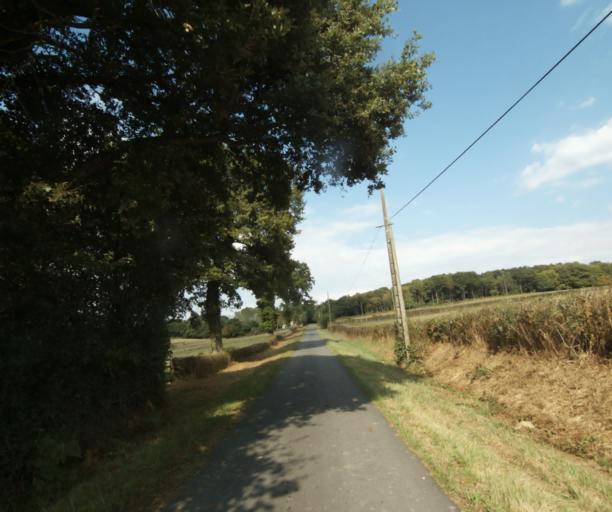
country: FR
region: Bourgogne
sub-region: Departement de Saone-et-Loire
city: Palinges
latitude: 46.5038
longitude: 4.2228
